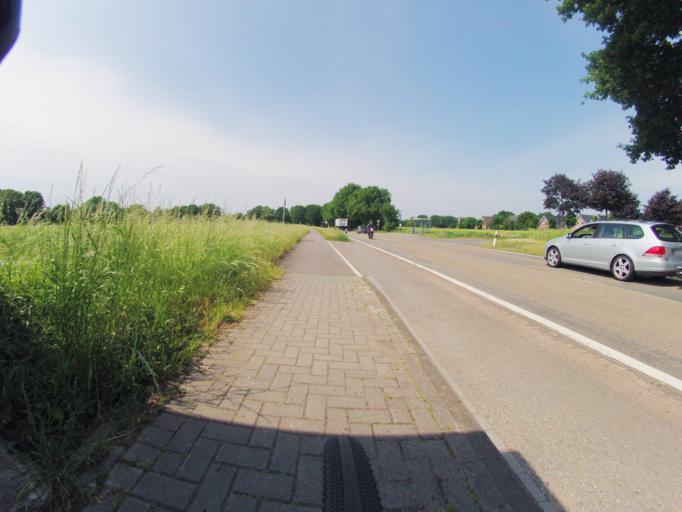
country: DE
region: North Rhine-Westphalia
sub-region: Regierungsbezirk Munster
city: Horstel
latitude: 52.3191
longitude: 7.6300
